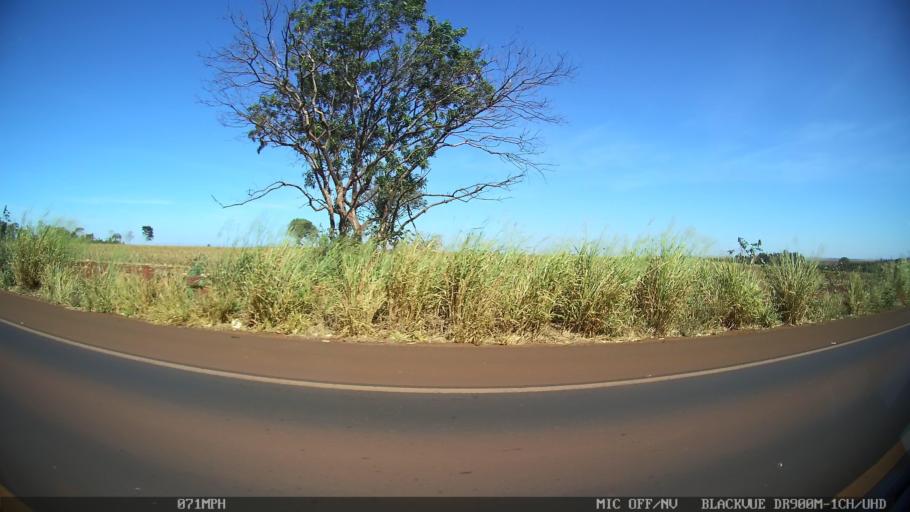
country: BR
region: Sao Paulo
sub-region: Guaira
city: Guaira
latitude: -20.4450
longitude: -48.3849
